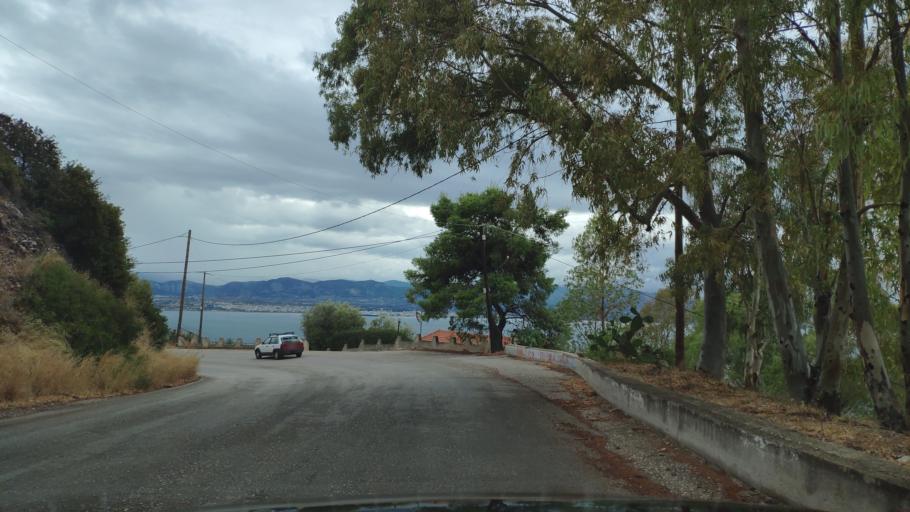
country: GR
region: Peloponnese
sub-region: Nomos Korinthias
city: Perachora
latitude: 38.0024
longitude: 22.9407
